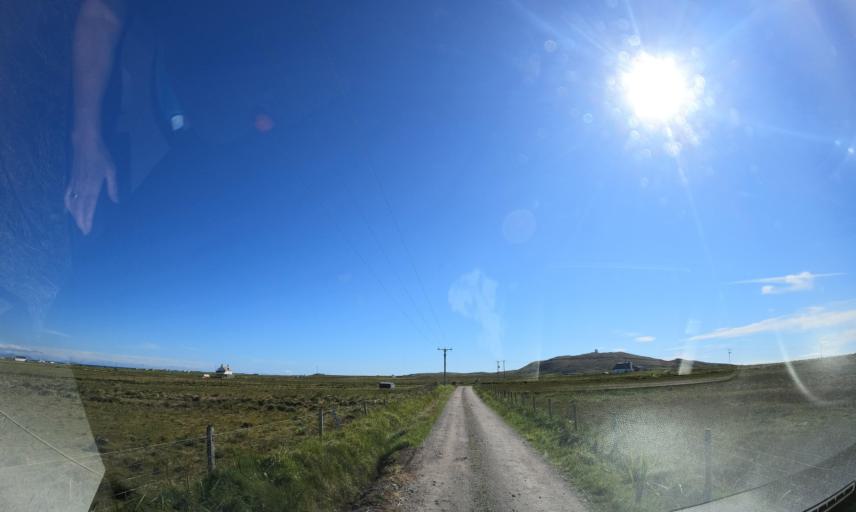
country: GB
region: Scotland
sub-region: Eilean Siar
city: Barra
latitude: 56.4749
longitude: -6.9186
